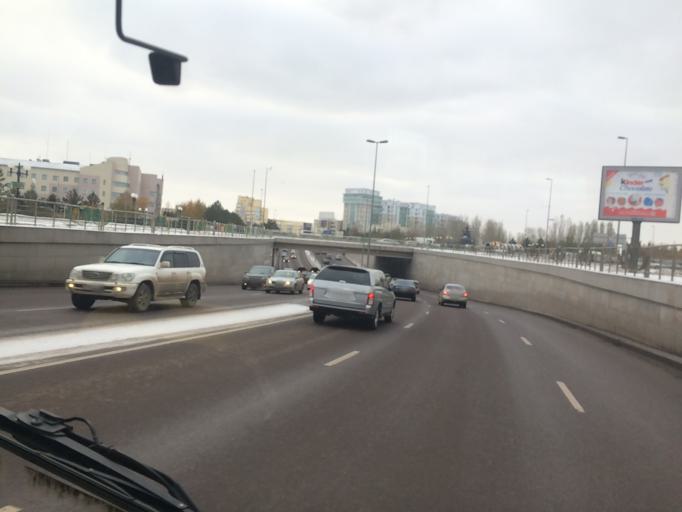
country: KZ
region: Astana Qalasy
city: Astana
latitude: 51.1550
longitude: 71.4302
